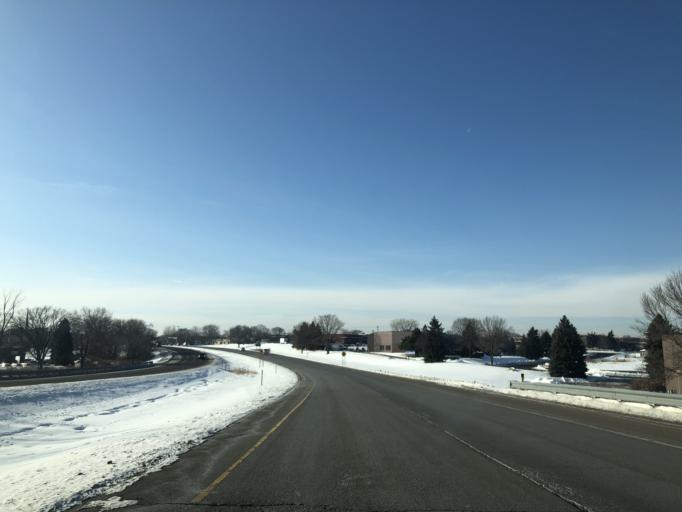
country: US
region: Minnesota
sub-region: Ramsey County
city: New Brighton
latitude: 45.0388
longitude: -93.1936
